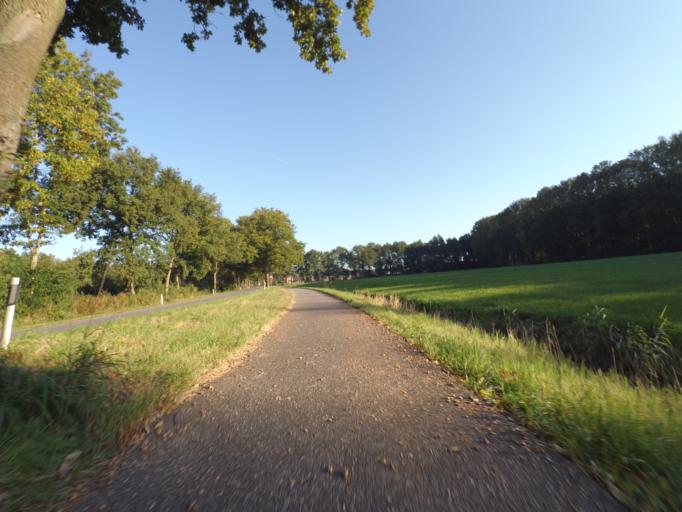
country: NL
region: Gelderland
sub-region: Gemeente Barneveld
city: Zwartebroek
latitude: 52.1979
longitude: 5.5257
